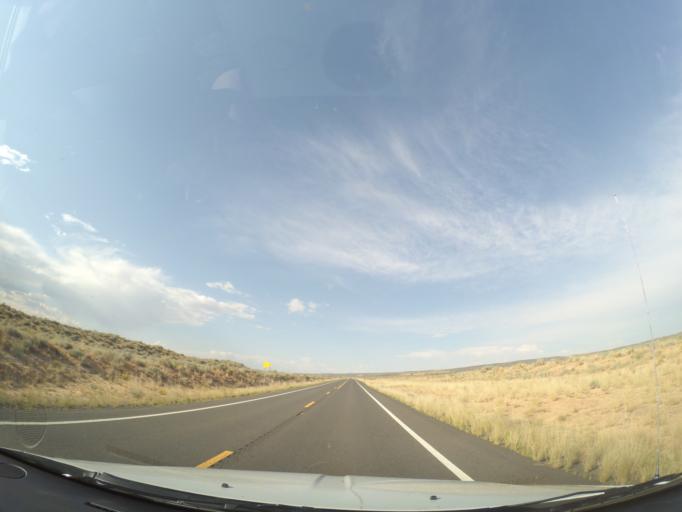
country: US
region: Arizona
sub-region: Coconino County
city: Kaibito
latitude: 36.4708
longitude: -111.4194
